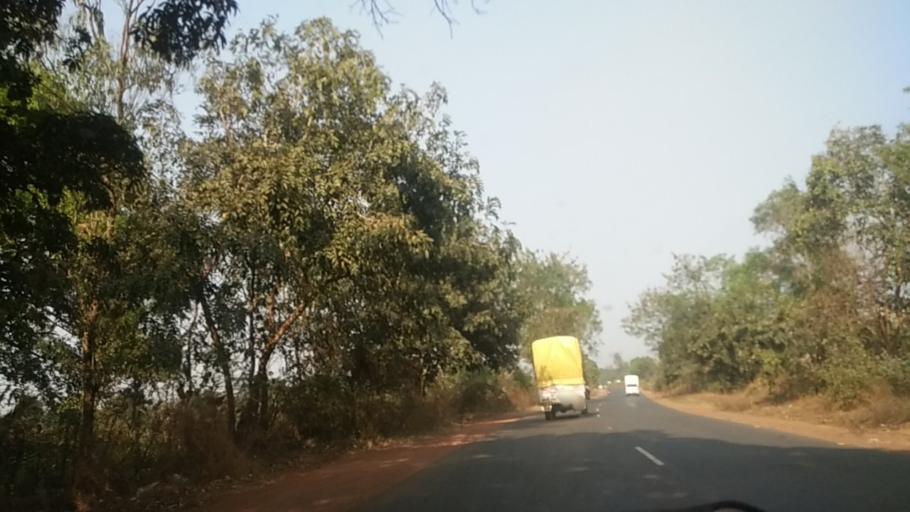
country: IN
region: Goa
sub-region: North Goa
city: Colovale
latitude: 15.6251
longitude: 73.8236
